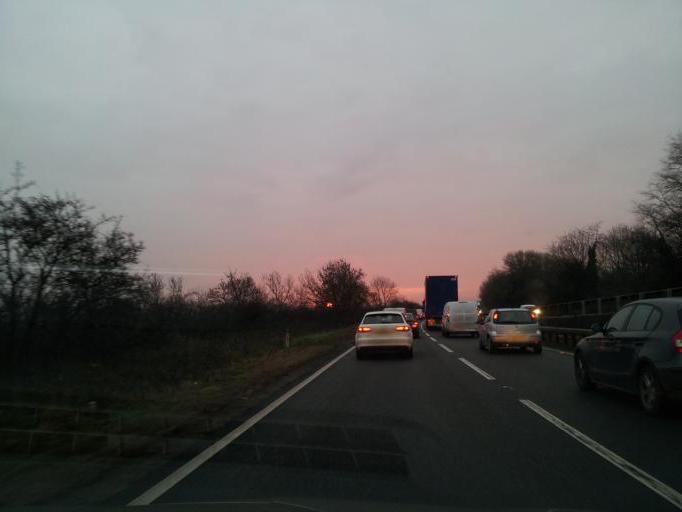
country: GB
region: England
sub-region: Peterborough
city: Wittering
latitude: 52.6099
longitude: -0.4350
